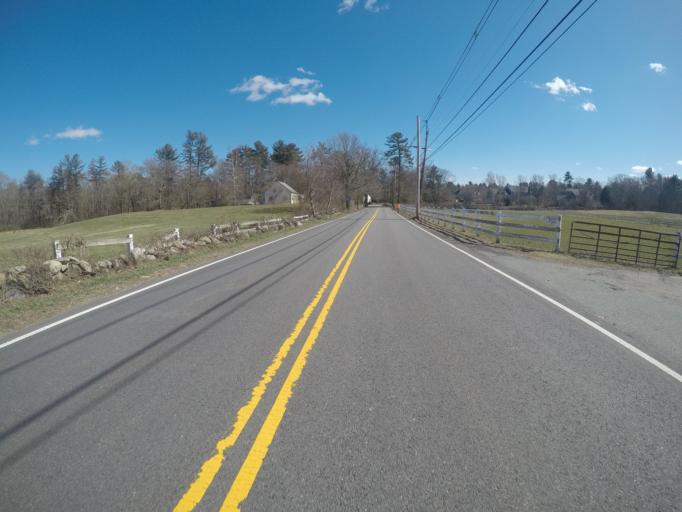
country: US
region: Massachusetts
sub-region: Bristol County
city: Easton
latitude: 42.0384
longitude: -71.1376
